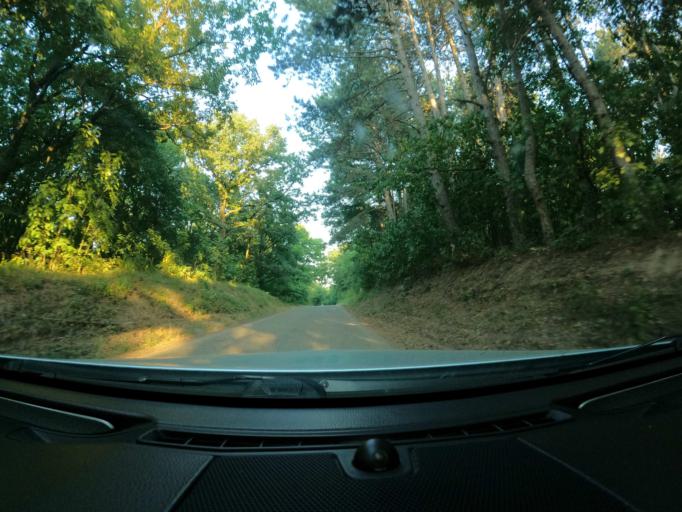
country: RS
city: Vrdnik
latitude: 45.1586
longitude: 19.7736
